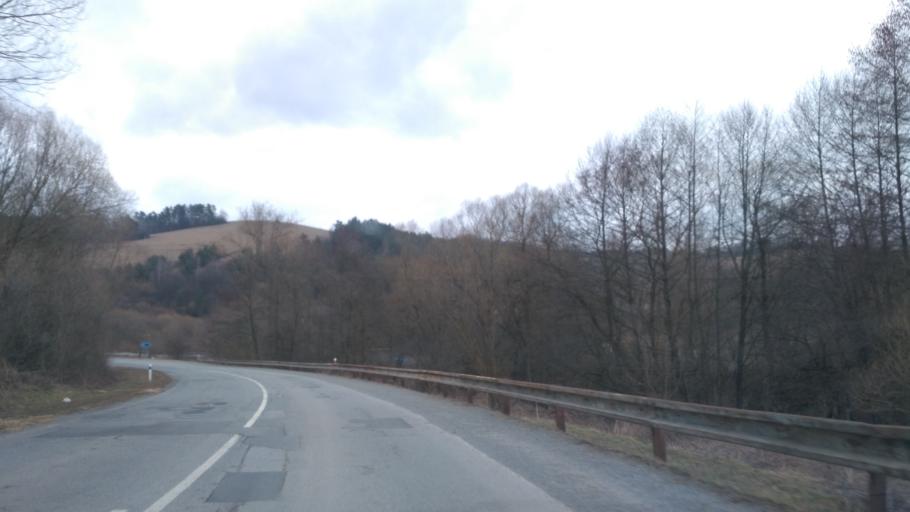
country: SK
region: Presovsky
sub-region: Okres Presov
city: Presov
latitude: 48.9591
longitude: 21.1145
